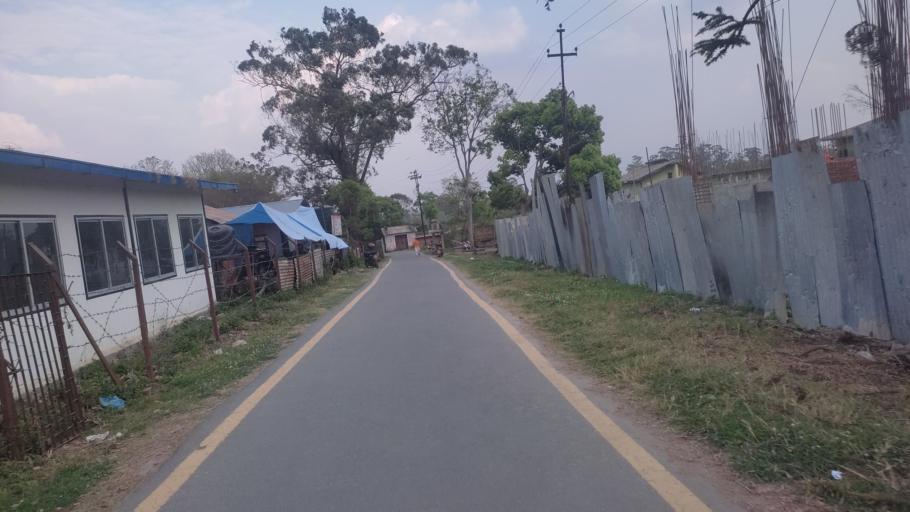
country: NP
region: Central Region
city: Kirtipur
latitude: 27.6814
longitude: 85.2846
